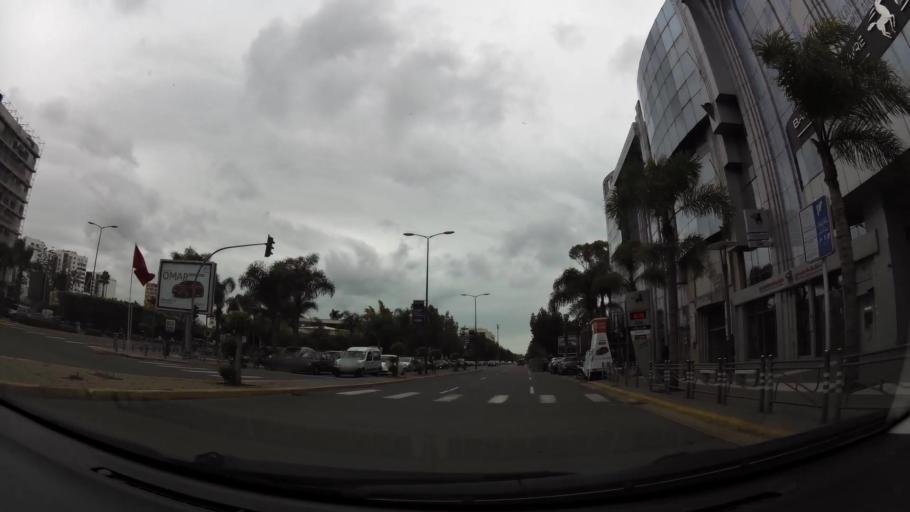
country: MA
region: Grand Casablanca
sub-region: Casablanca
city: Casablanca
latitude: 33.5881
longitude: -7.6444
